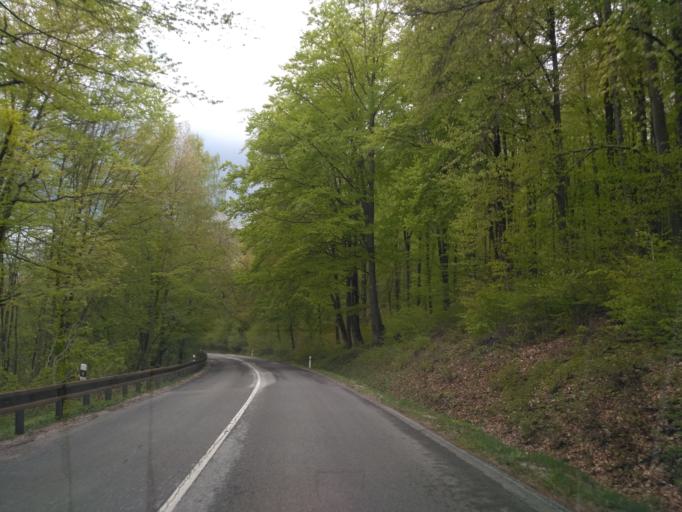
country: SK
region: Kosicky
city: Dobsina
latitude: 48.6410
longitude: 20.3042
